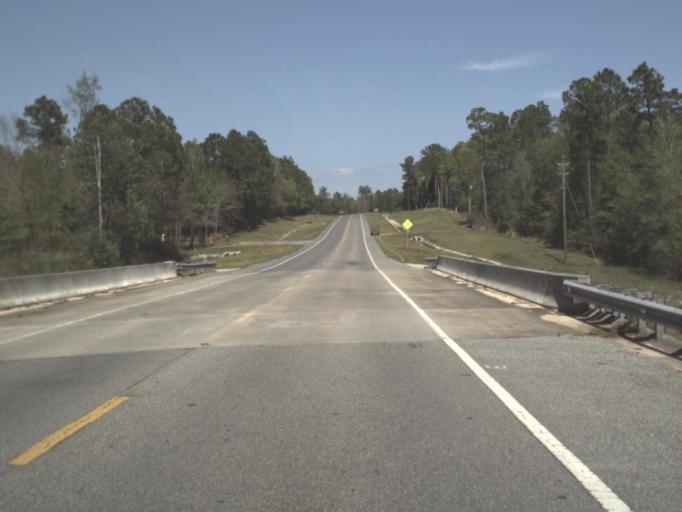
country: US
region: Florida
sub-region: Okaloosa County
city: Crestview
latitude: 30.7276
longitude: -86.6604
